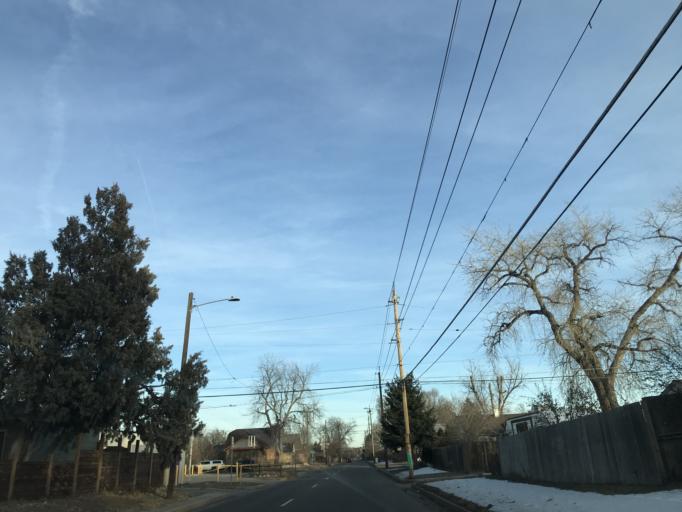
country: US
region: Colorado
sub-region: Arapahoe County
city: Glendale
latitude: 39.7387
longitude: -104.8963
